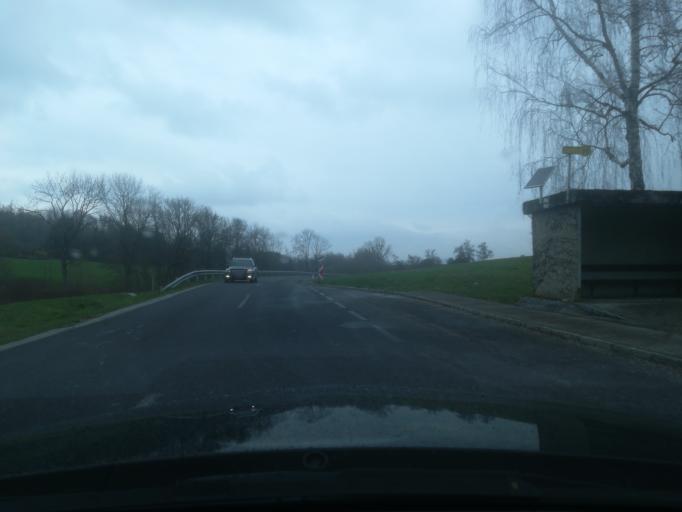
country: AT
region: Upper Austria
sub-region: Wels-Land
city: Buchkirchen
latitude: 48.2598
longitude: 14.0350
